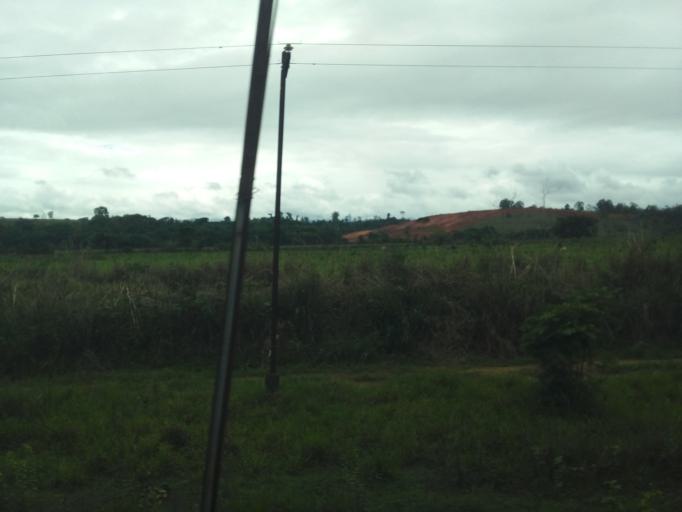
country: BR
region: Minas Gerais
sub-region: Ipatinga
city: Ipatinga
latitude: -19.4723
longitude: -42.4830
